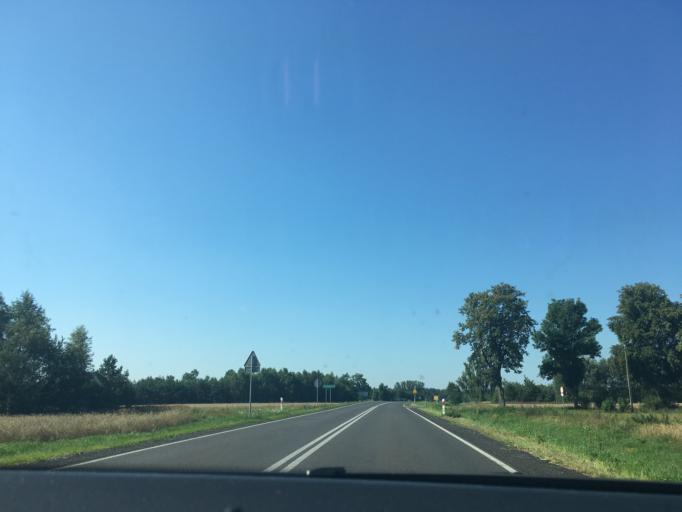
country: PL
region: Lublin Voivodeship
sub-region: Powiat lubartowski
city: Kock
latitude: 51.6770
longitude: 22.4856
